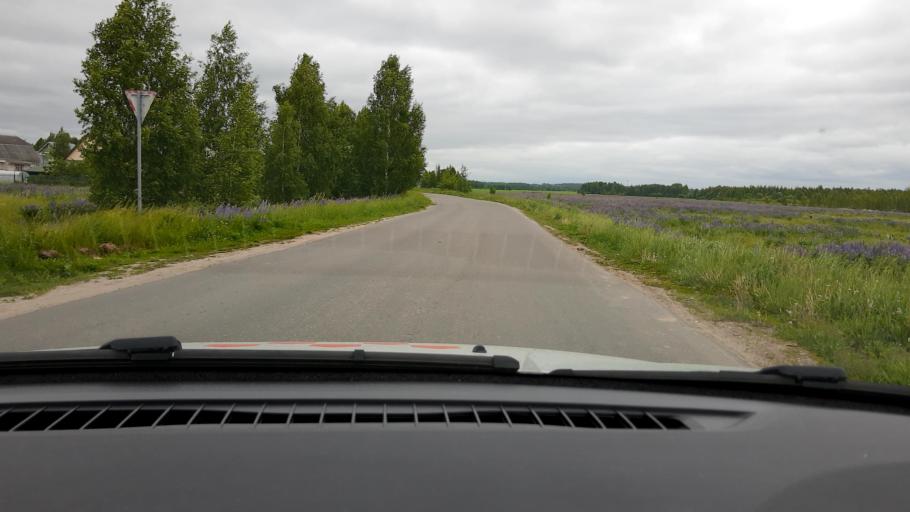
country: RU
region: Nizjnij Novgorod
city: Sitniki
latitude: 56.5244
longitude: 44.0404
